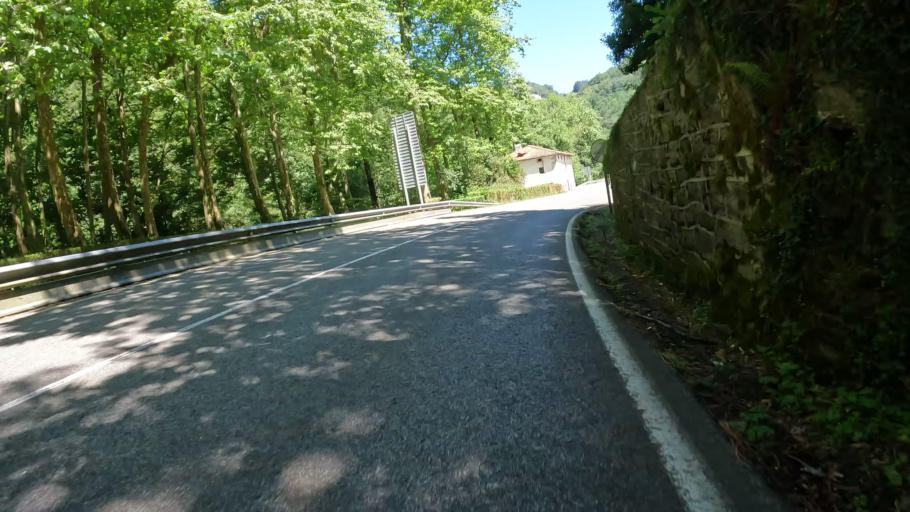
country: ES
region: Basque Country
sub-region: Provincia de Guipuzcoa
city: Oreja
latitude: 43.0703
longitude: -2.0115
